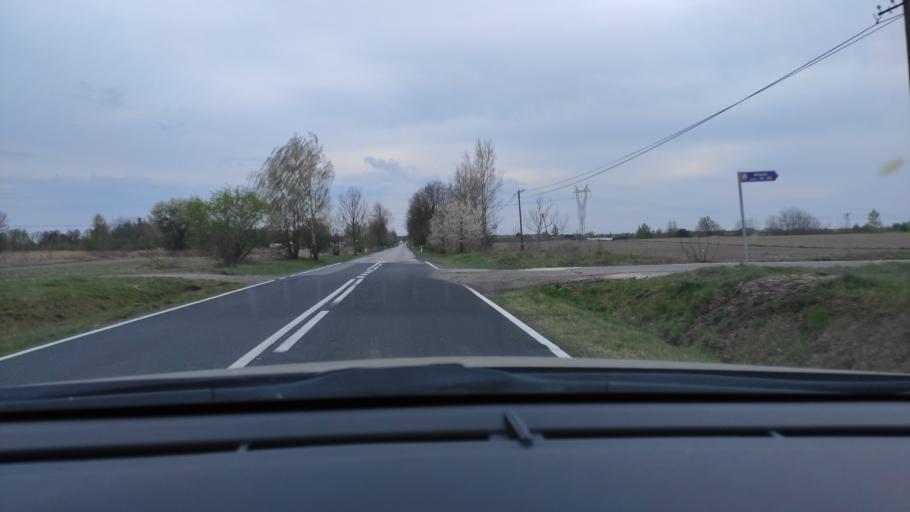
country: PL
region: Masovian Voivodeship
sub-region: Powiat zwolenski
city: Zwolen
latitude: 51.3696
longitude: 21.5637
